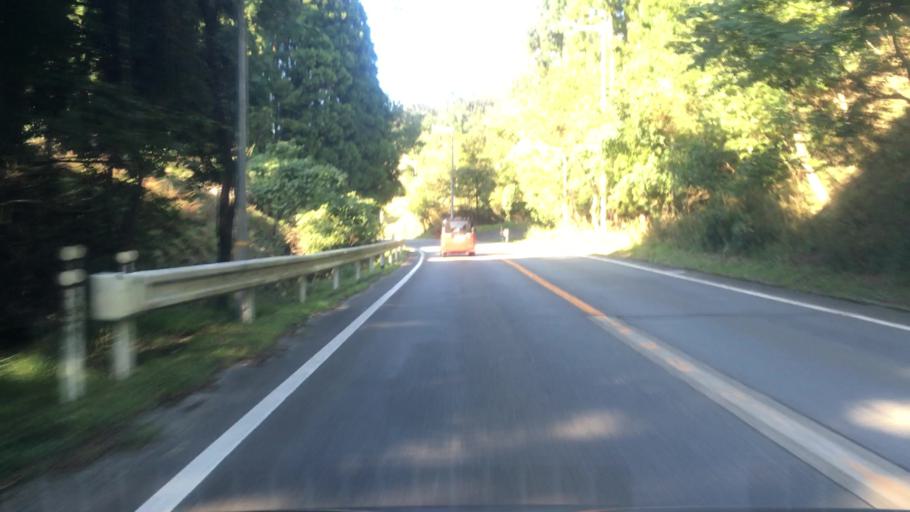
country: JP
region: Hyogo
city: Toyooka
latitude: 35.5654
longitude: 134.8527
